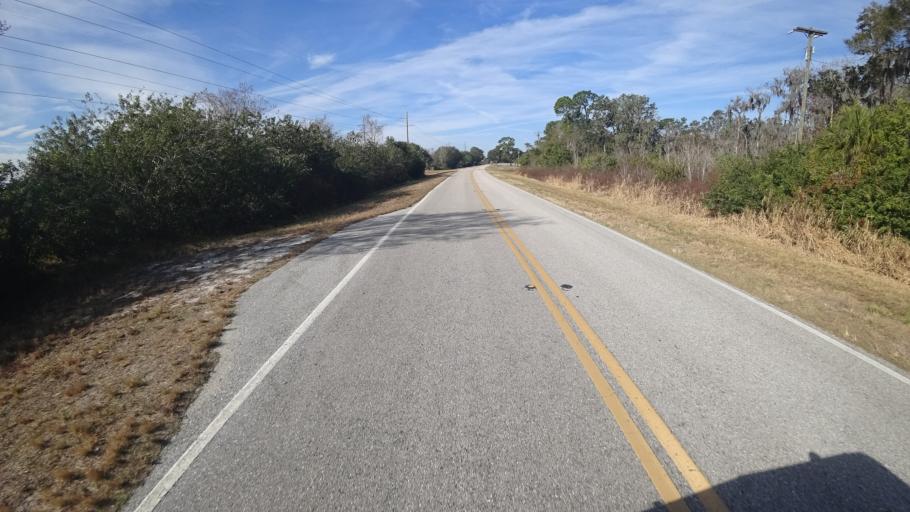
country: US
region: Florida
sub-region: Hillsborough County
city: Ruskin
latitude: 27.6234
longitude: -82.4807
